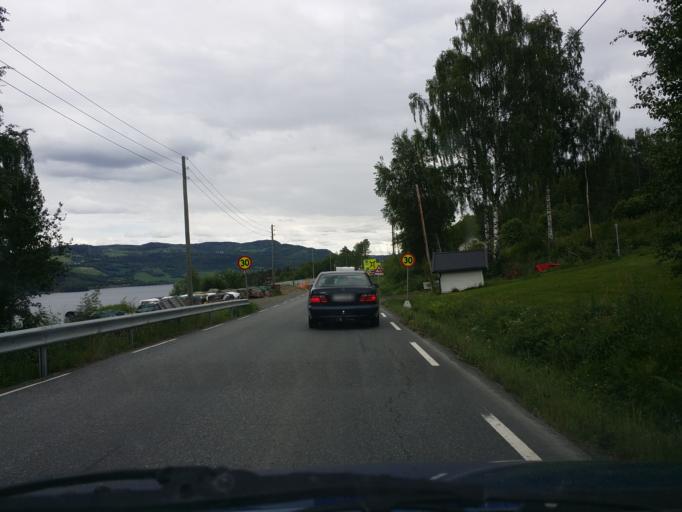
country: NO
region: Hedmark
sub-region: Ringsaker
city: Moelv
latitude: 60.9850
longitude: 10.5598
